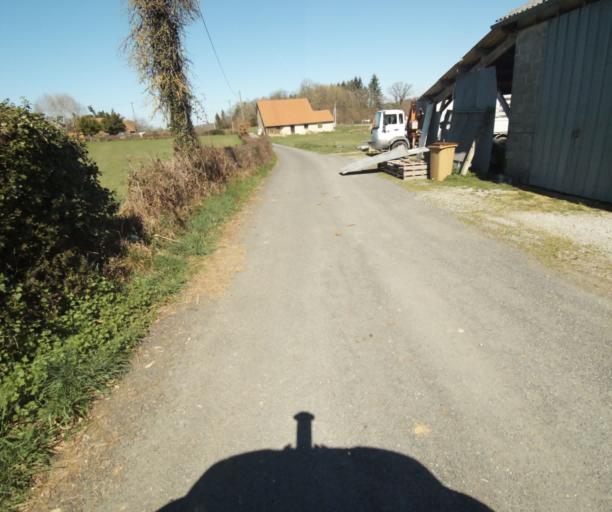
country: FR
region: Limousin
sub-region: Departement de la Correze
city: Saint-Mexant
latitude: 45.3102
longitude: 1.6420
